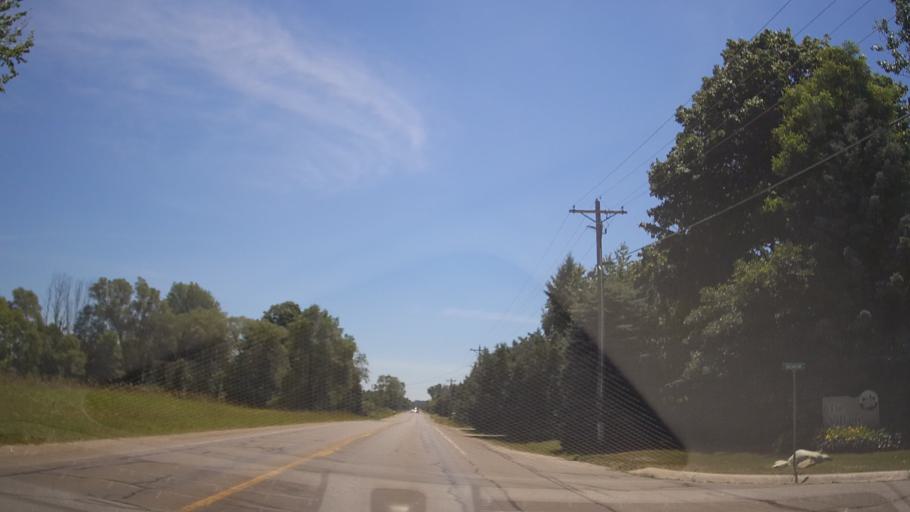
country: US
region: Michigan
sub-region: Grand Traverse County
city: Traverse City
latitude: 44.6794
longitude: -85.6897
